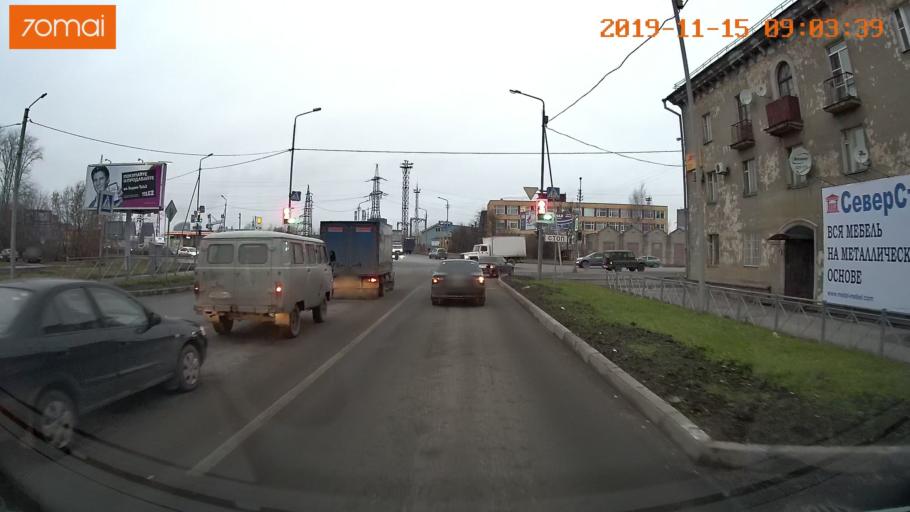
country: RU
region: Vologda
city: Cherepovets
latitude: 59.1394
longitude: 37.9196
